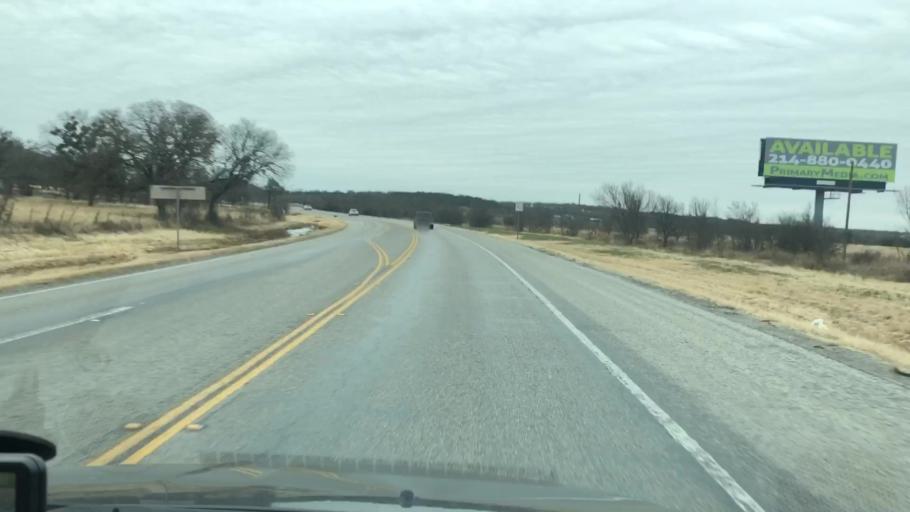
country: US
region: Texas
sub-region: Palo Pinto County
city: Mineral Wells
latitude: 32.8557
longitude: -98.0935
